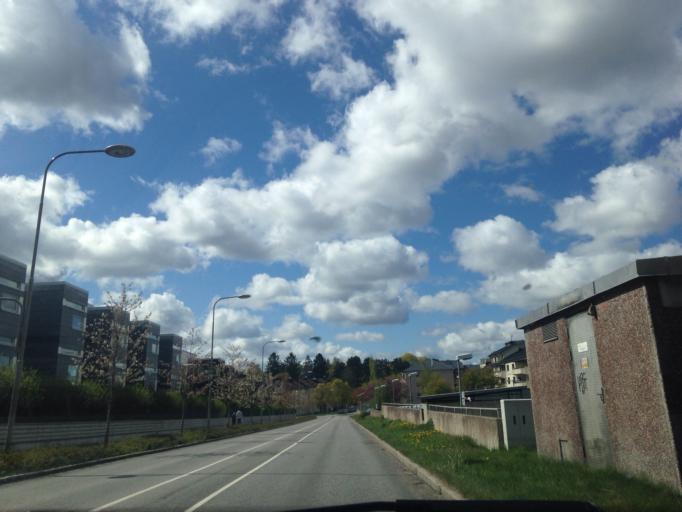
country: SE
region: Stockholm
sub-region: Stockholms Kommun
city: Arsta
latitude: 59.2860
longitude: 18.1009
